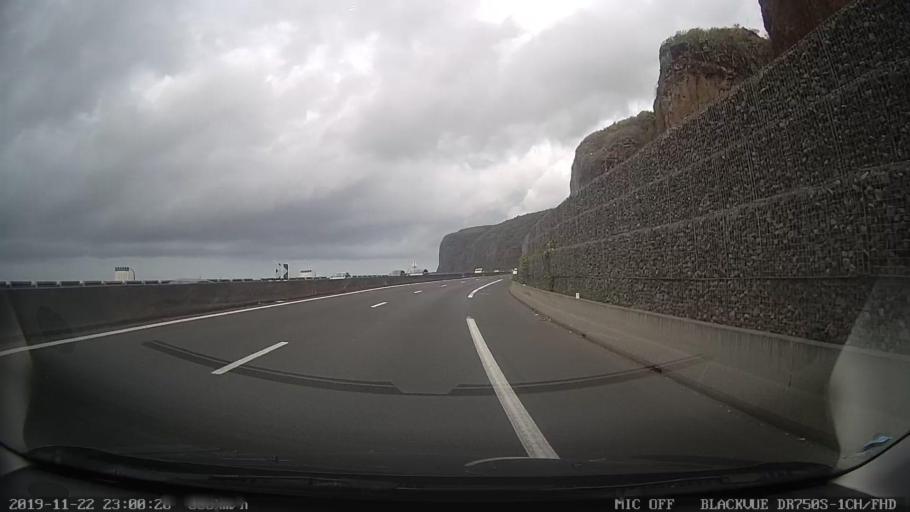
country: RE
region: Reunion
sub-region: Reunion
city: La Possession
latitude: -20.9104
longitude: 55.3520
